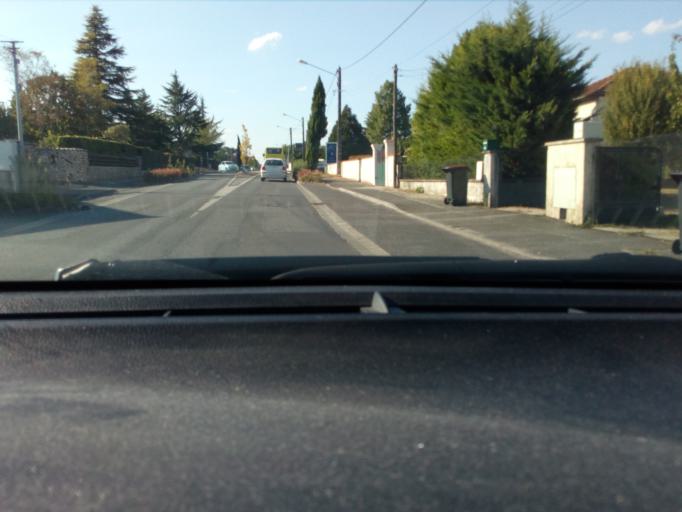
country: FR
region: Poitou-Charentes
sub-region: Departement de la Charente
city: Saint-Yrieix-sur-Charente
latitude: 45.6757
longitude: 0.1226
